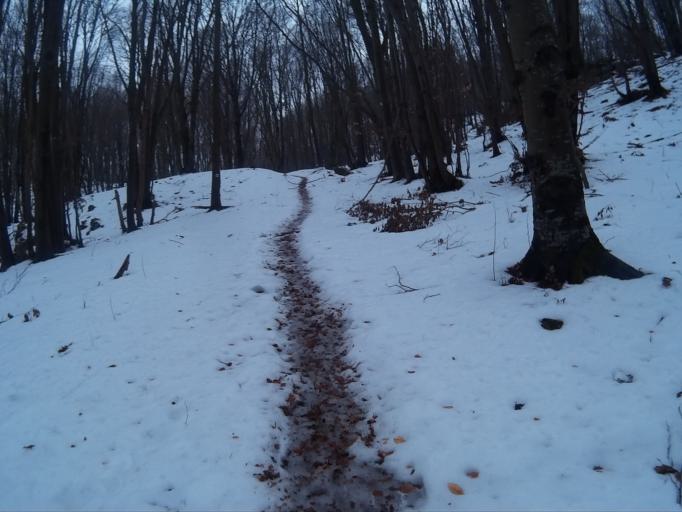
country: HU
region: Heves
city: Belapatfalva
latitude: 48.0480
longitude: 20.4022
